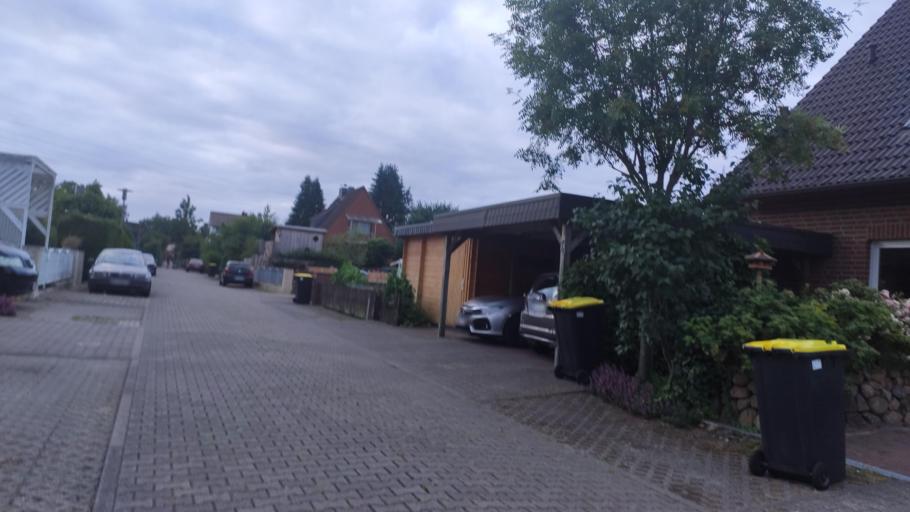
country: DE
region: Schleswig-Holstein
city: Geesthacht
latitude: 53.4421
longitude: 10.3551
